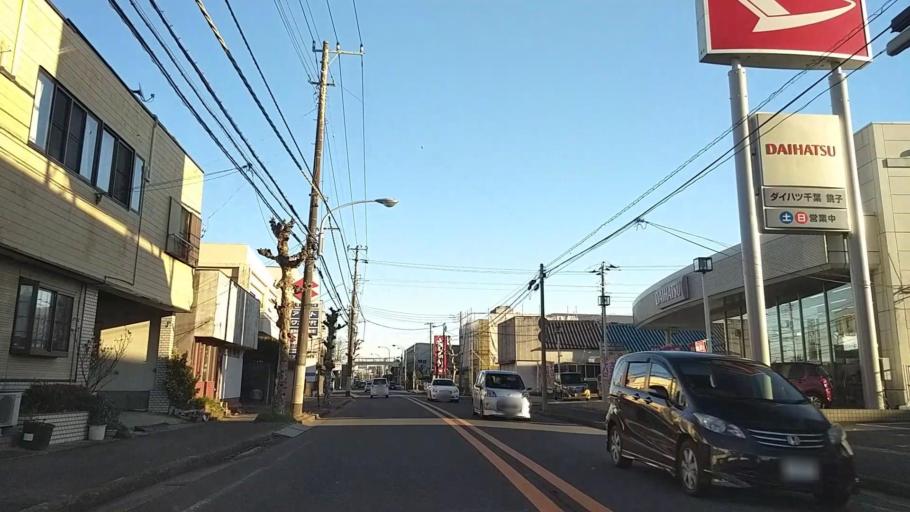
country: JP
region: Chiba
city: Hasaki
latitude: 35.7396
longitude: 140.7987
